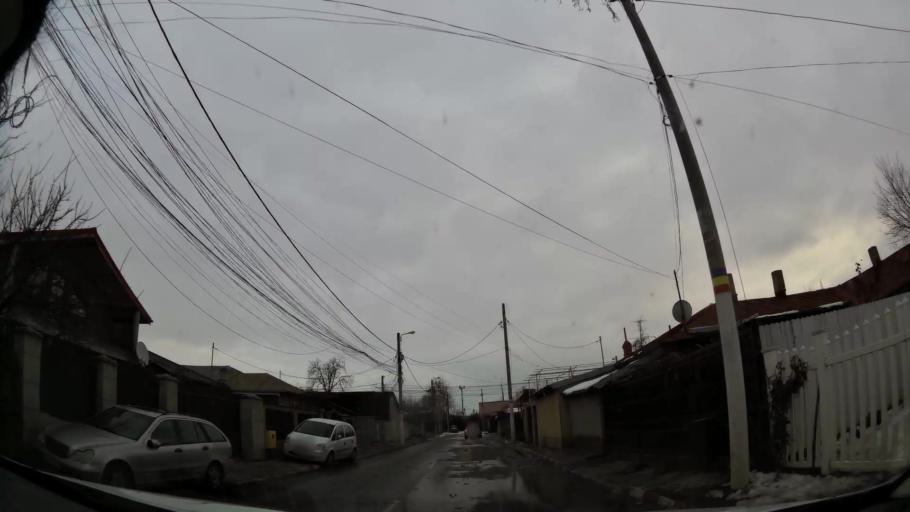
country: RO
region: Ilfov
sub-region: Voluntari City
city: Voluntari
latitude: 44.4830
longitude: 26.1706
